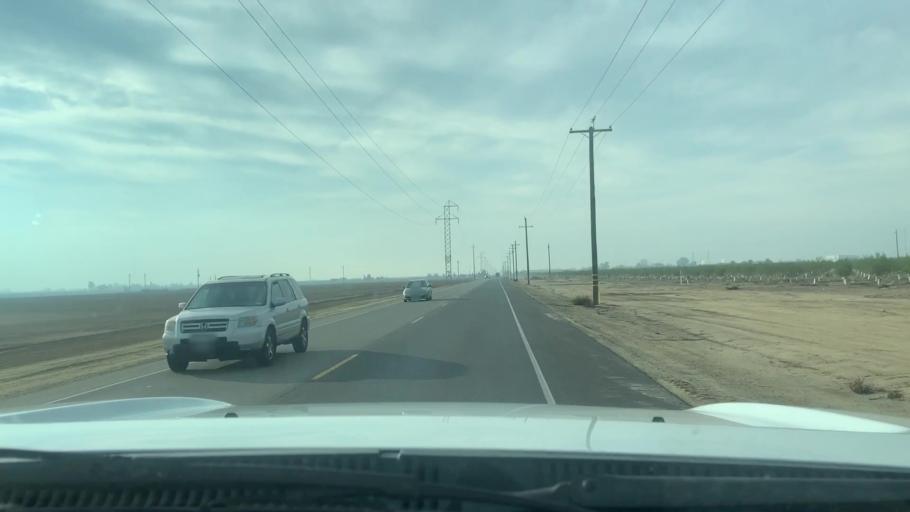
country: US
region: California
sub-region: Kern County
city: Shafter
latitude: 35.4417
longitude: -119.2320
